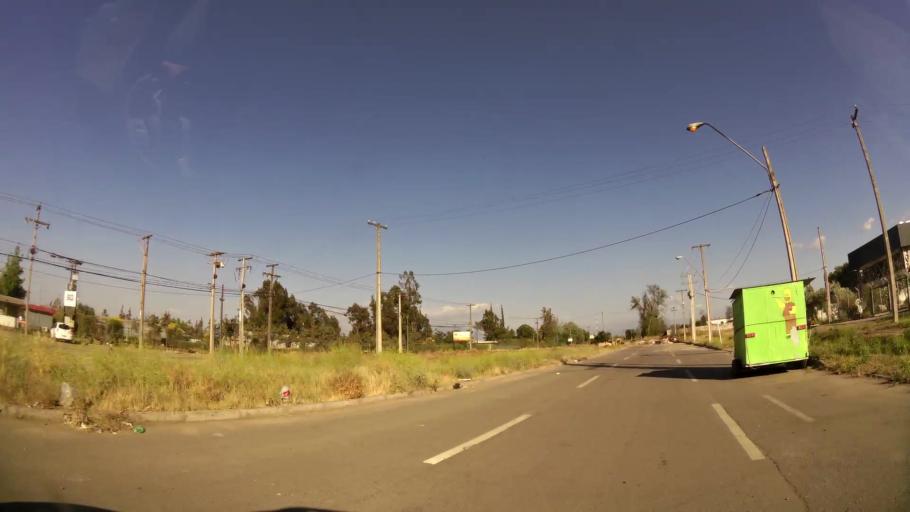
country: CL
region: Santiago Metropolitan
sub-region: Provincia de Maipo
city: San Bernardo
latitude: -33.5404
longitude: -70.7649
